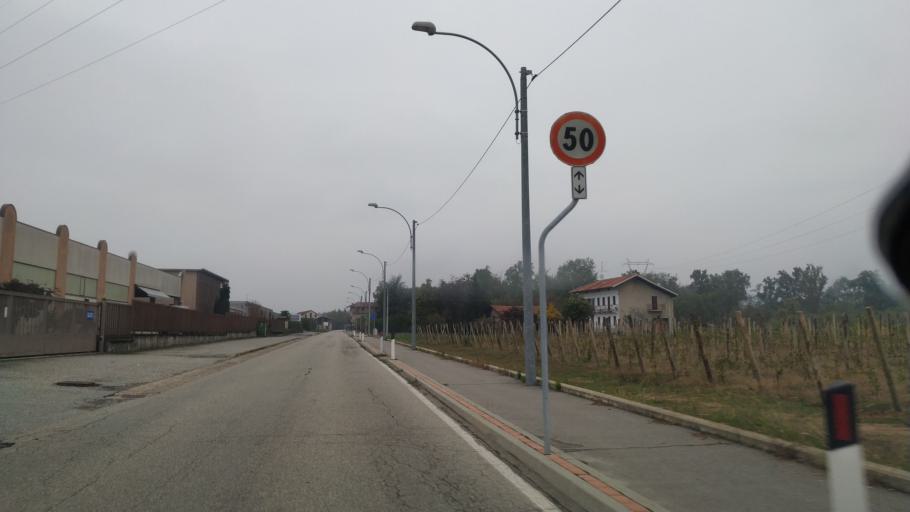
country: IT
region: Piedmont
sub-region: Provincia di Biella
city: Lessona
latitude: 45.5719
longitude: 8.2079
